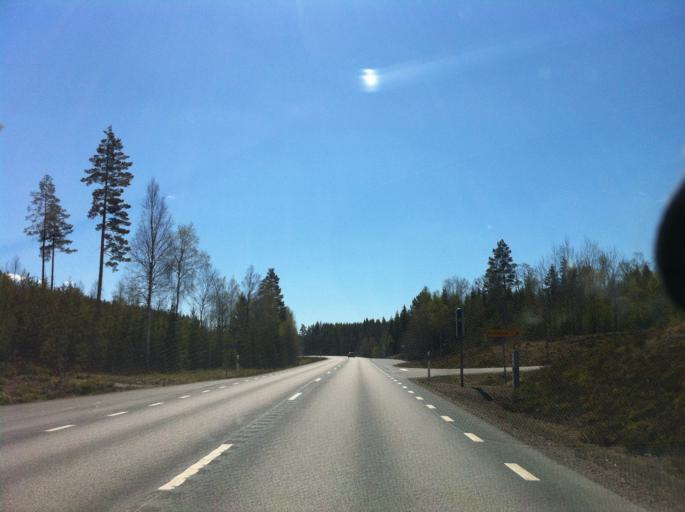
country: SE
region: Kalmar
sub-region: Vimmerby Kommun
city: Vimmerby
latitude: 57.6318
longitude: 15.8384
